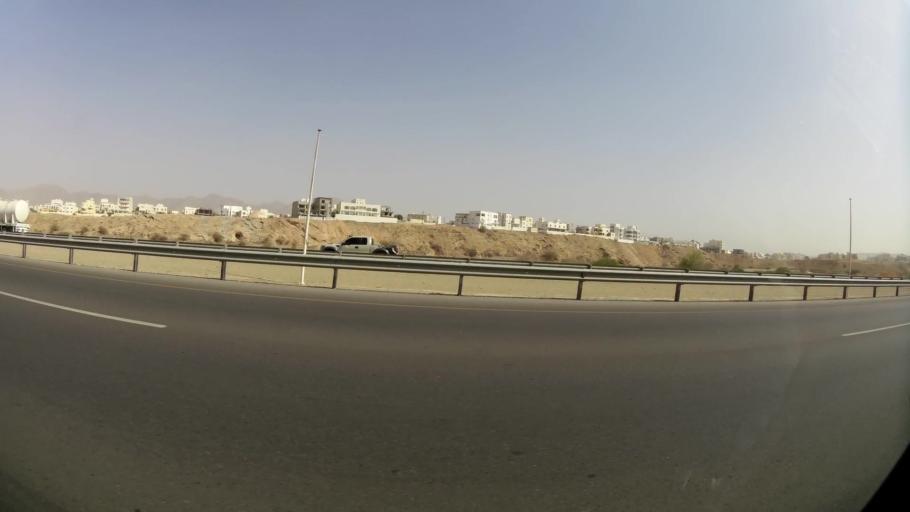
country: OM
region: Muhafazat Masqat
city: Bawshar
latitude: 23.5652
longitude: 58.3571
